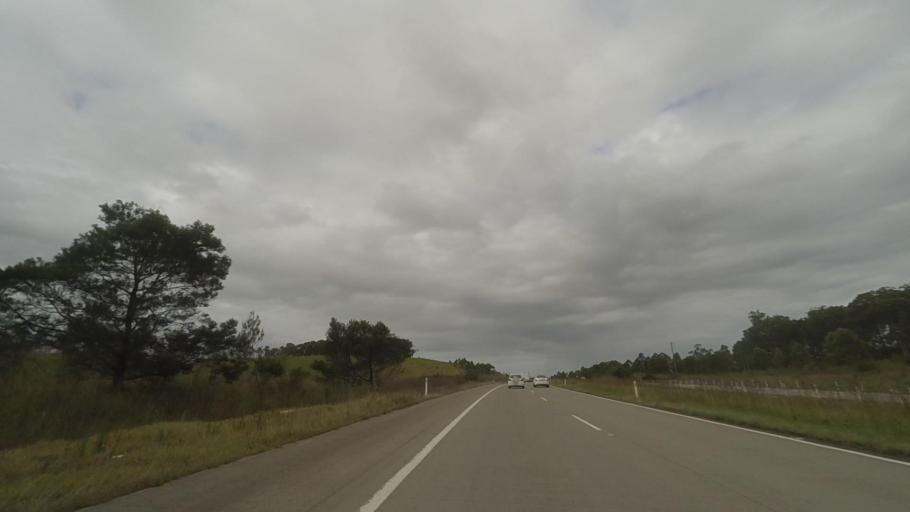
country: AU
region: New South Wales
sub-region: Port Stephens Shire
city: Port Stephens
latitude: -32.6334
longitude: 152.0434
